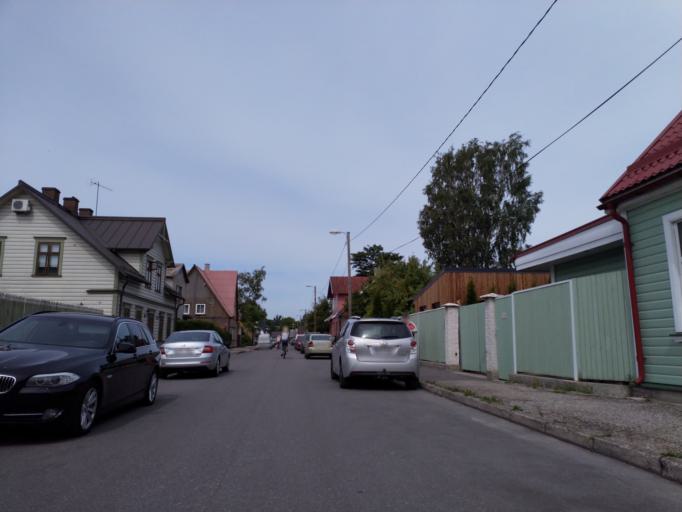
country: EE
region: Paernumaa
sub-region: Paernu linn
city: Parnu
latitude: 58.3795
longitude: 24.5184
